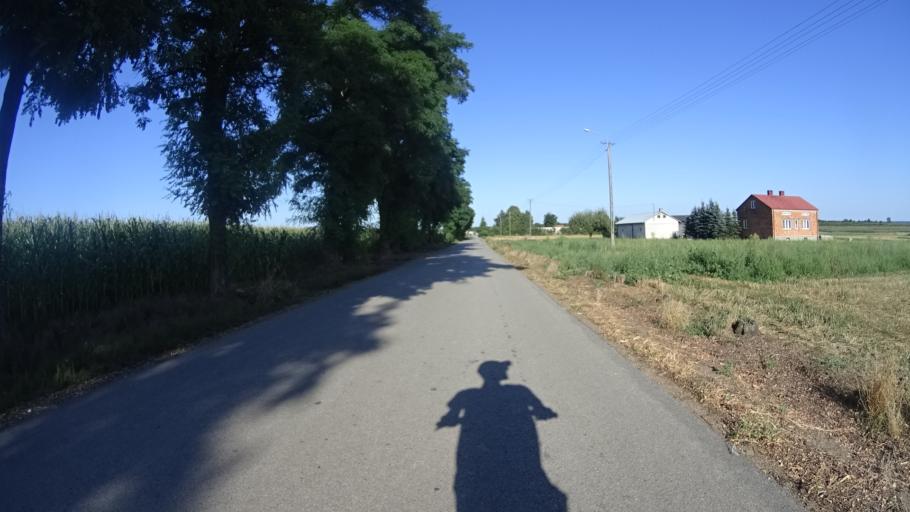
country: PL
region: Masovian Voivodeship
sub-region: Powiat bialobrzeski
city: Wysmierzyce
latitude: 51.6713
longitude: 20.8190
